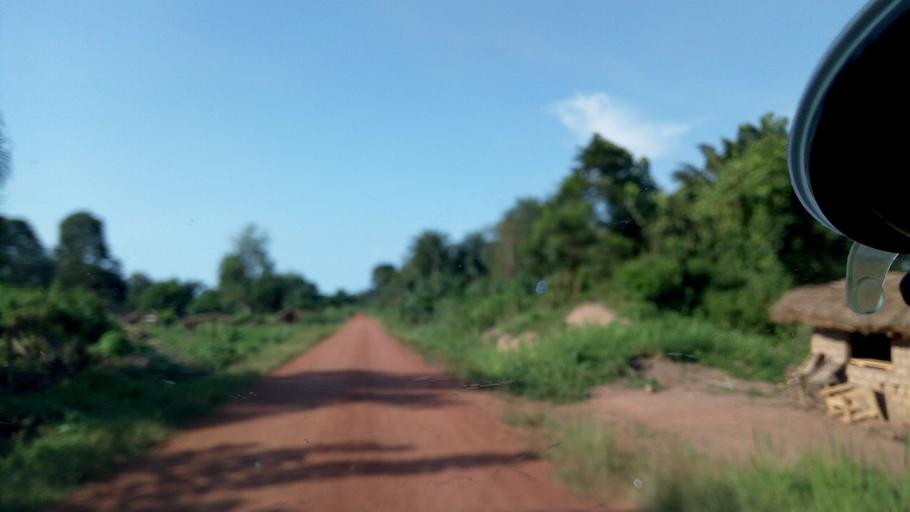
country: CD
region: Equateur
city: Libenge
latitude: 3.9330
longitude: 18.6984
